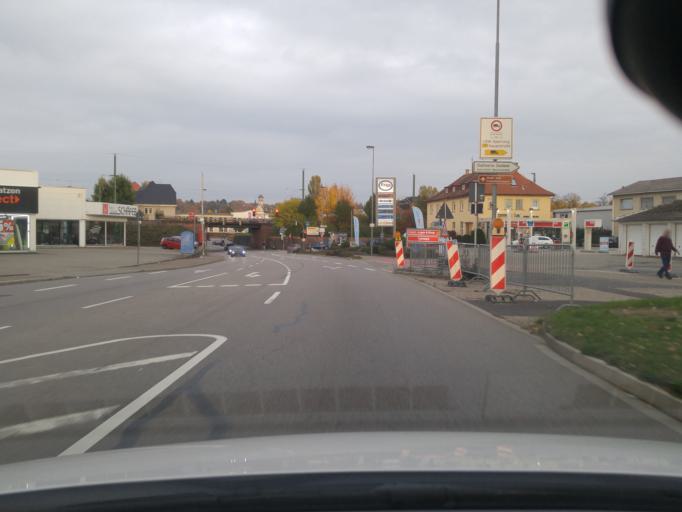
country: DE
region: Baden-Wuerttemberg
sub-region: Karlsruhe Region
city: Sinsheim
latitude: 49.2510
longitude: 8.8689
